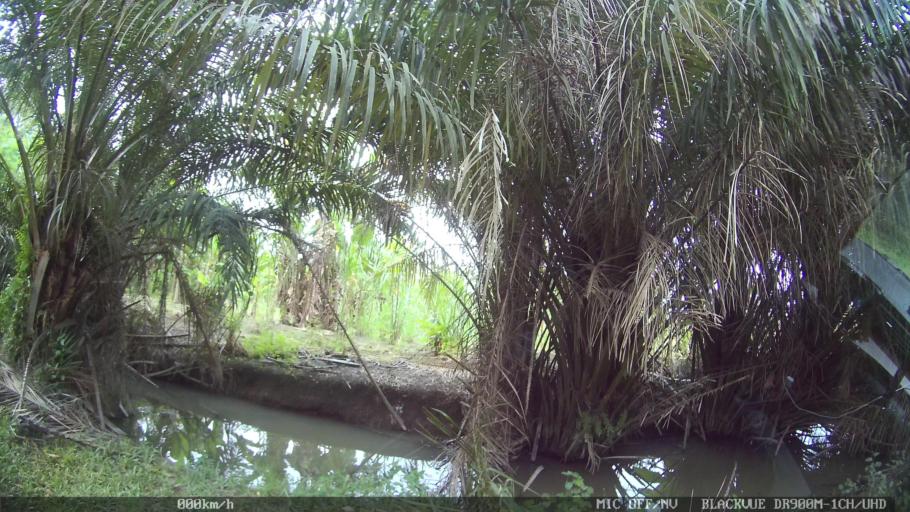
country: ID
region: North Sumatra
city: Medan
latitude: 3.5734
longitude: 98.7461
